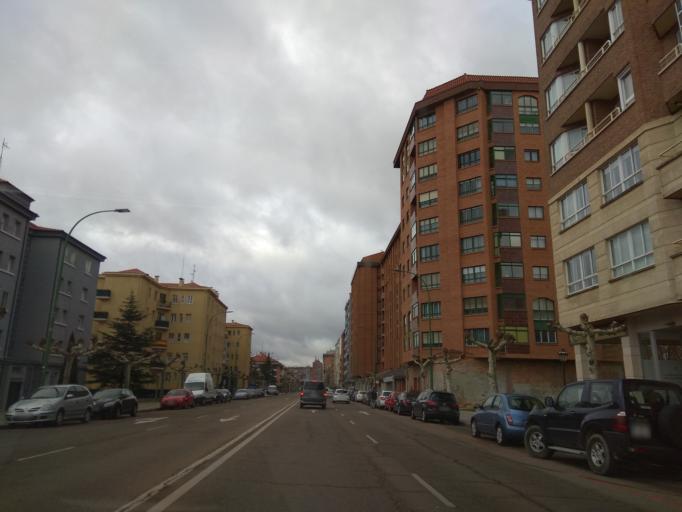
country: ES
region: Castille and Leon
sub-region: Provincia de Burgos
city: Burgos
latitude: 42.3478
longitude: -3.6791
